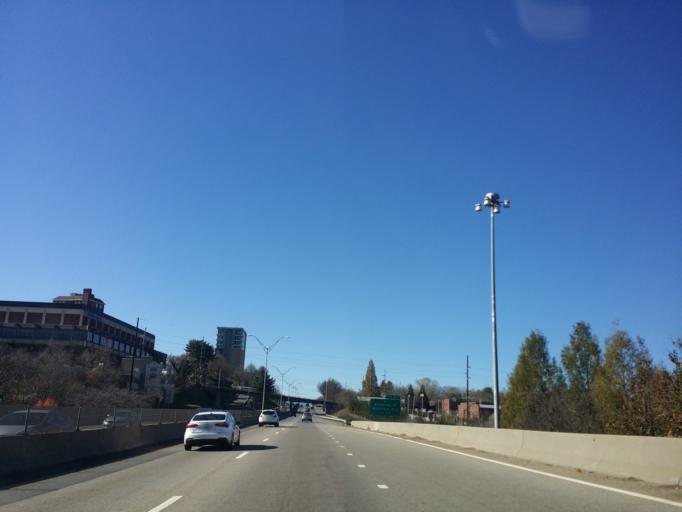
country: US
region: North Carolina
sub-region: Buncombe County
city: Asheville
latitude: 35.5997
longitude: -82.5536
